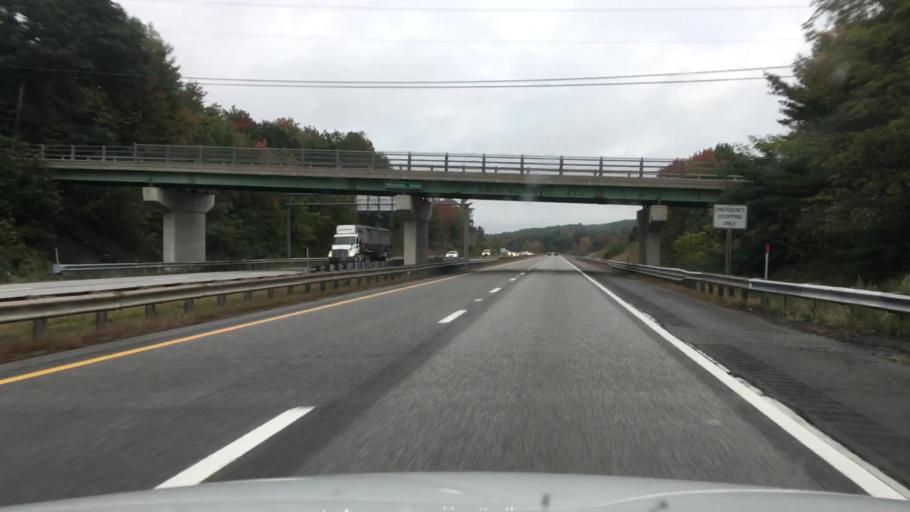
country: US
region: Maine
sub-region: Cumberland County
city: Falmouth
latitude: 43.7463
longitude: -70.3030
